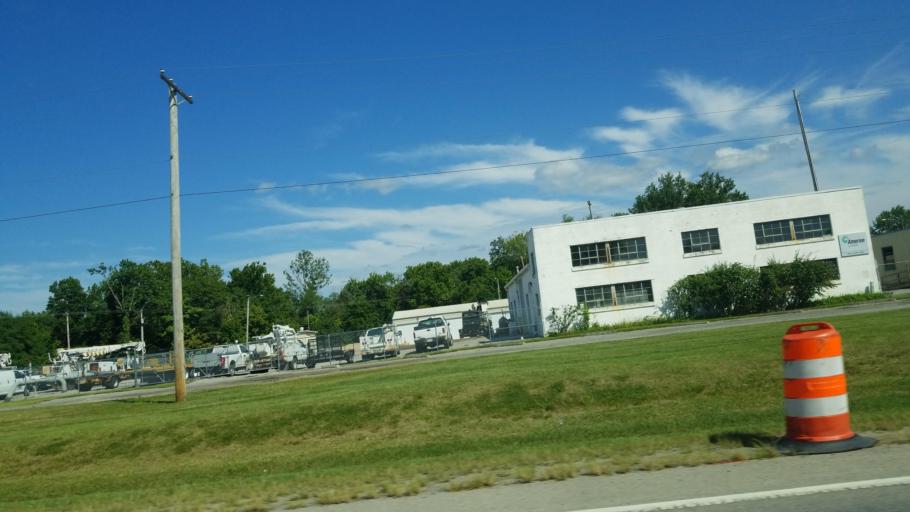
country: US
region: Illinois
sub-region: Williamson County
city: Marion
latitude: 37.7475
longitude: -88.9327
